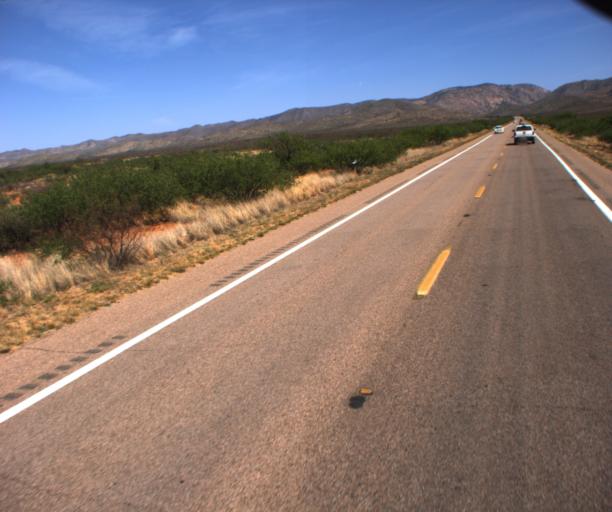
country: US
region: Arizona
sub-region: Cochise County
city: Bisbee
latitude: 31.5325
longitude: -110.0593
